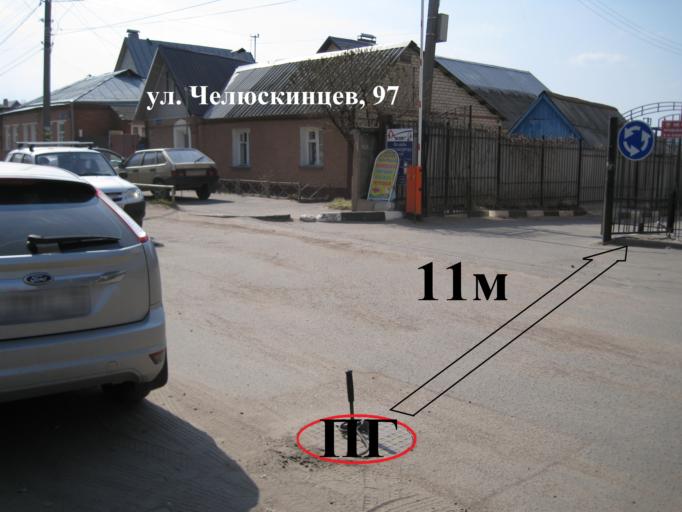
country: RU
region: Voronezj
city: Voronezh
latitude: 51.6484
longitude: 39.1923
